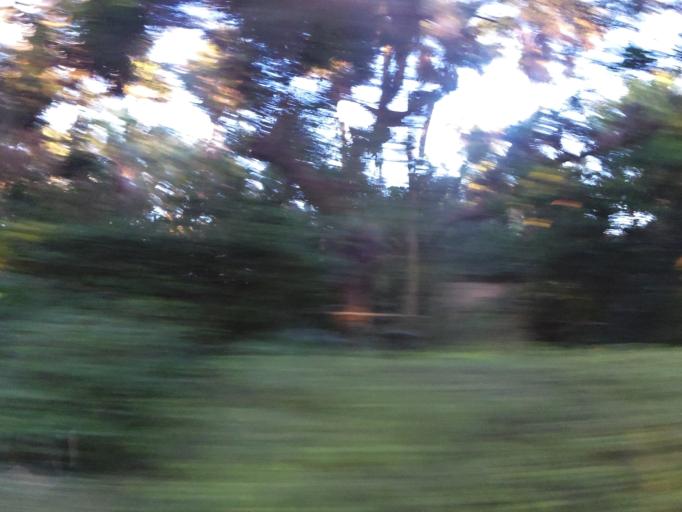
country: US
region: Florida
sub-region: Saint Johns County
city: Sawgrass
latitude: 30.1667
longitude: -81.3583
